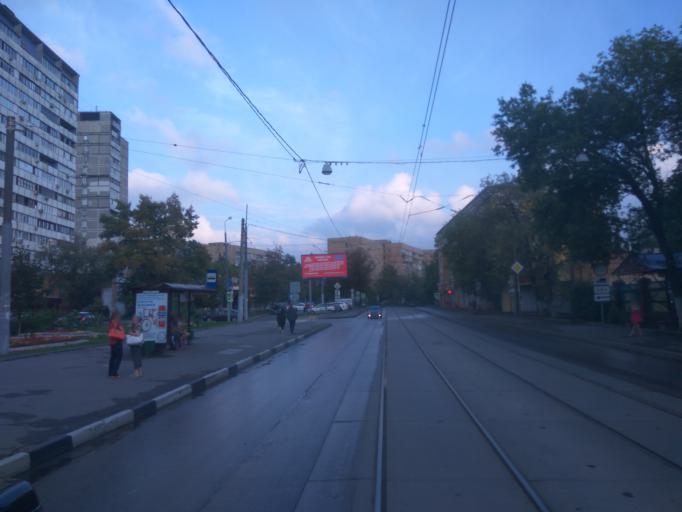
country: RU
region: Moskovskaya
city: Bogorodskoye
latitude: 55.8100
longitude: 37.7037
